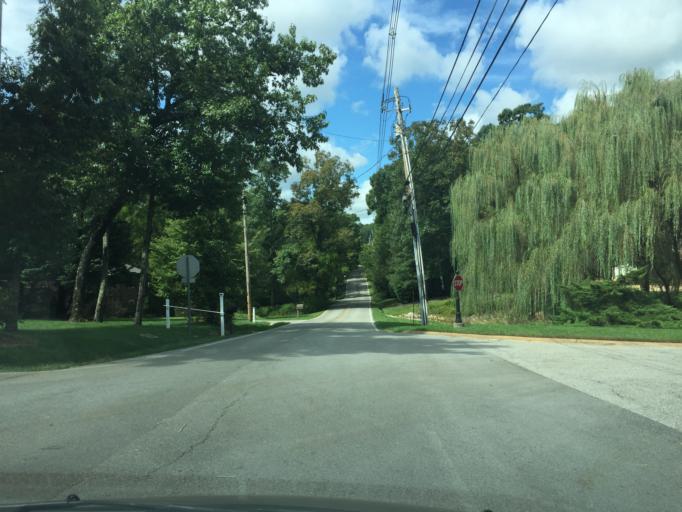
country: US
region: Tennessee
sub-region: Hamilton County
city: Signal Mountain
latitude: 35.1360
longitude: -85.3263
